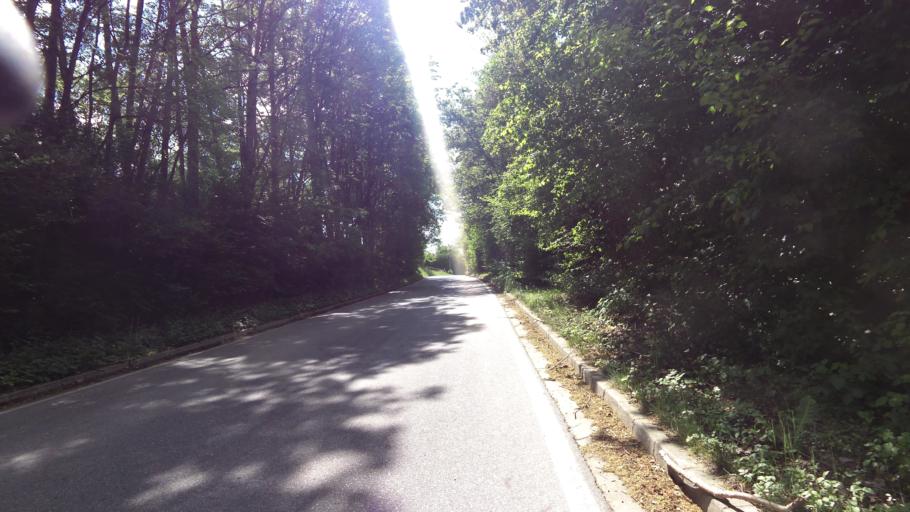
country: DE
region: Bavaria
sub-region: Upper Bavaria
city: Moosburg
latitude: 48.4883
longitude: 11.9248
